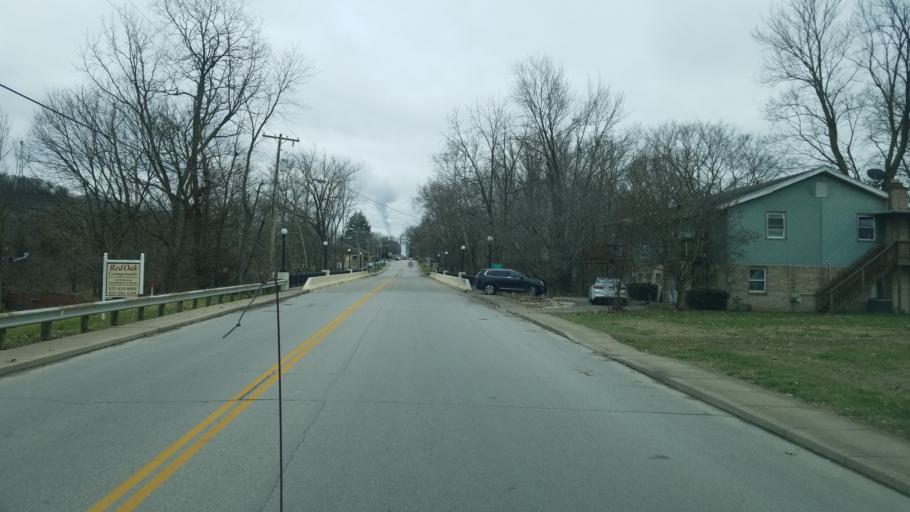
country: US
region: Ohio
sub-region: Brown County
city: Ripley
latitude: 38.7444
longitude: -83.8446
